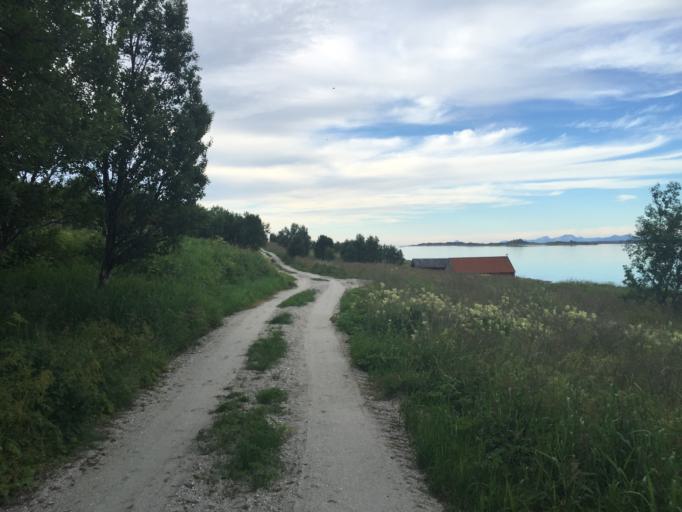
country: NO
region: Nordland
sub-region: Vagan
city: Kabelvag
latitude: 68.3284
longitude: 14.3967
